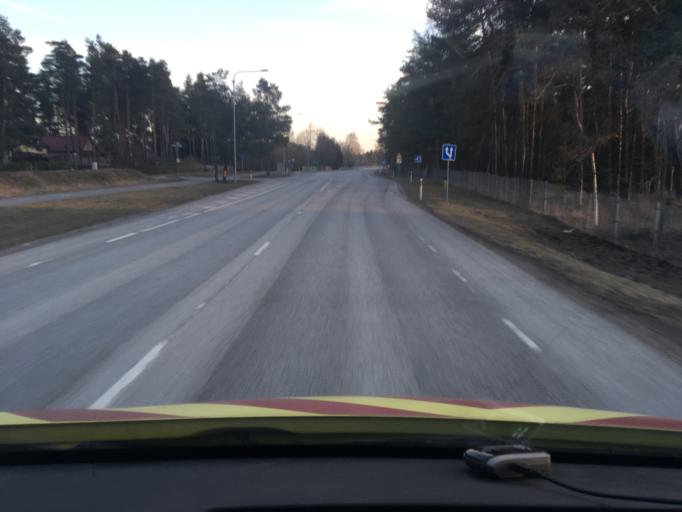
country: EE
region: Harju
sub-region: Kiili vald
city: Kiili
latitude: 59.3343
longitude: 24.7738
